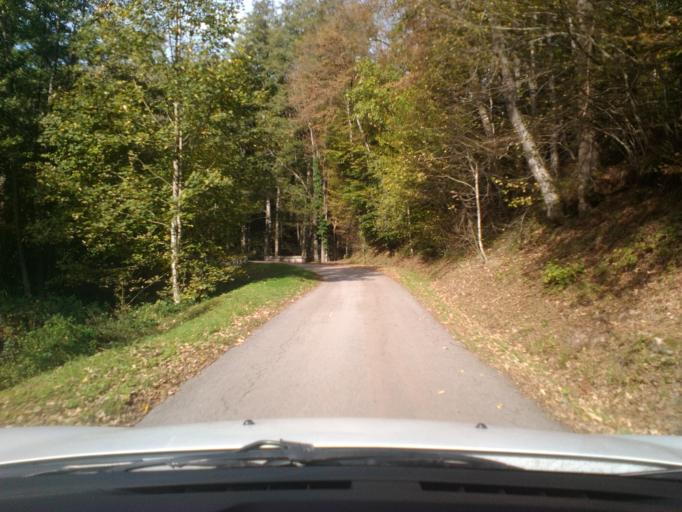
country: FR
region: Lorraine
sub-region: Departement des Vosges
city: Sainte-Marguerite
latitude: 48.2967
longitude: 7.0133
